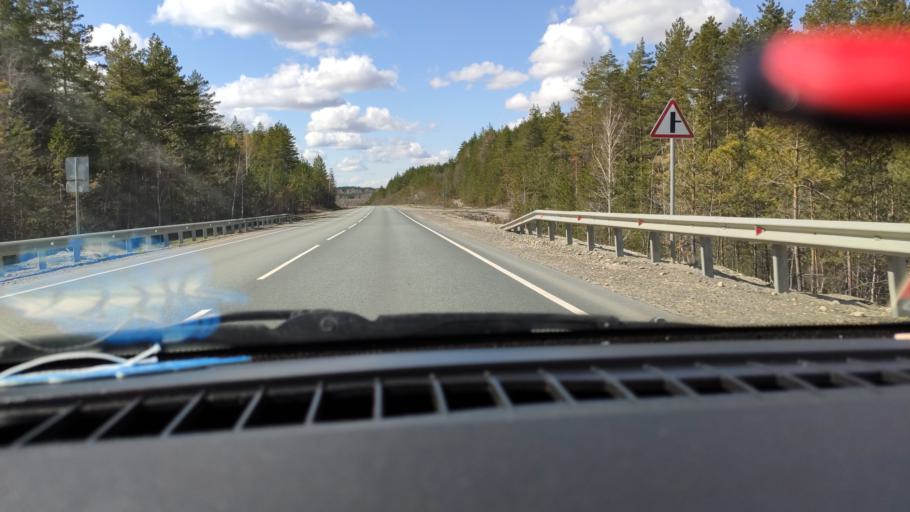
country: RU
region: Saratov
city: Khvalynsk
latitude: 52.5307
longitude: 48.0298
